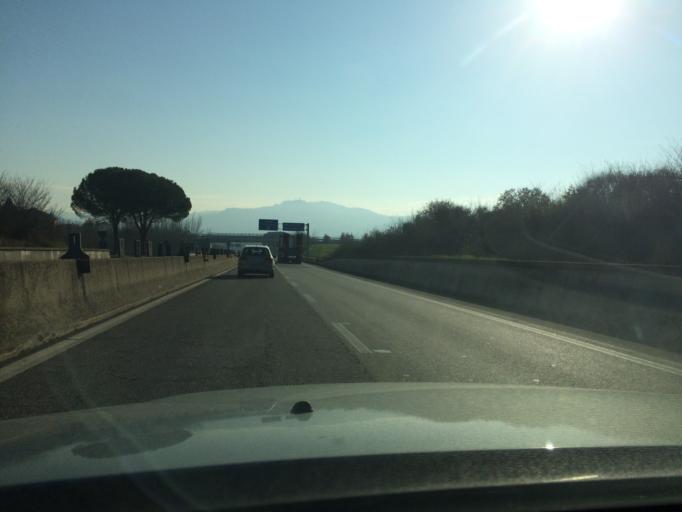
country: IT
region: Umbria
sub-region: Provincia di Perugia
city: Ponterio-Pian di Porto
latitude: 42.8229
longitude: 12.3992
